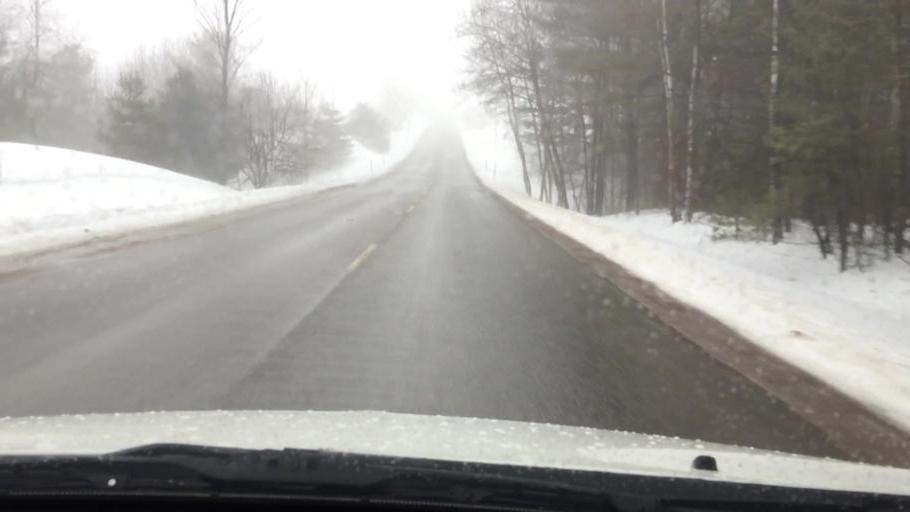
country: US
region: Michigan
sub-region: Charlevoix County
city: East Jordan
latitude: 45.1270
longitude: -85.1801
